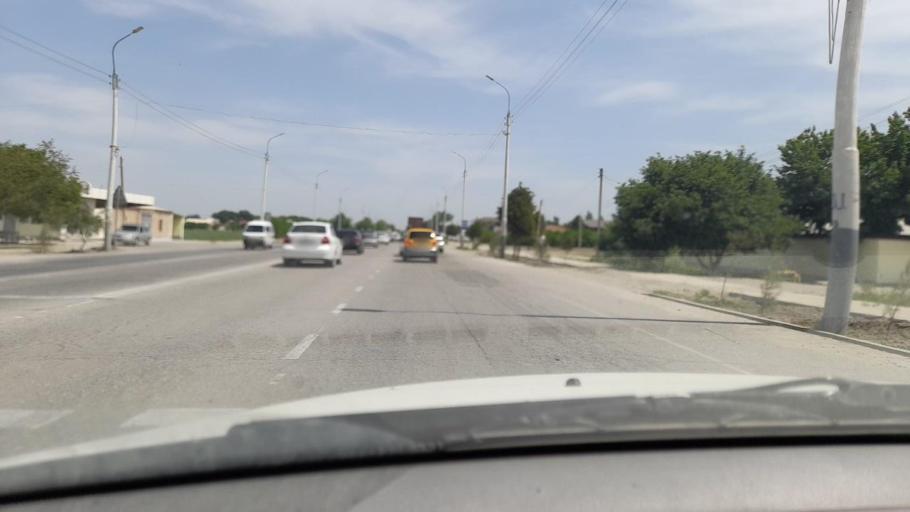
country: UZ
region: Navoiy
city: Karmana Shahri
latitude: 40.1471
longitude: 65.3291
